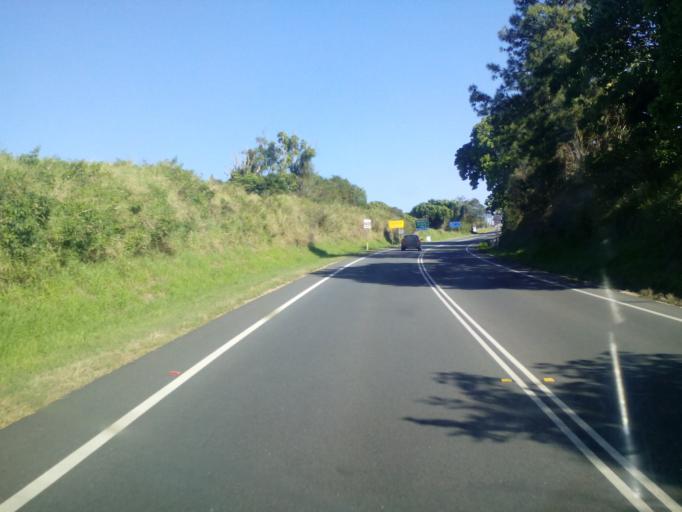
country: AU
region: New South Wales
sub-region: Tweed
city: Kingscliff
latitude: -28.2622
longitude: 153.5620
